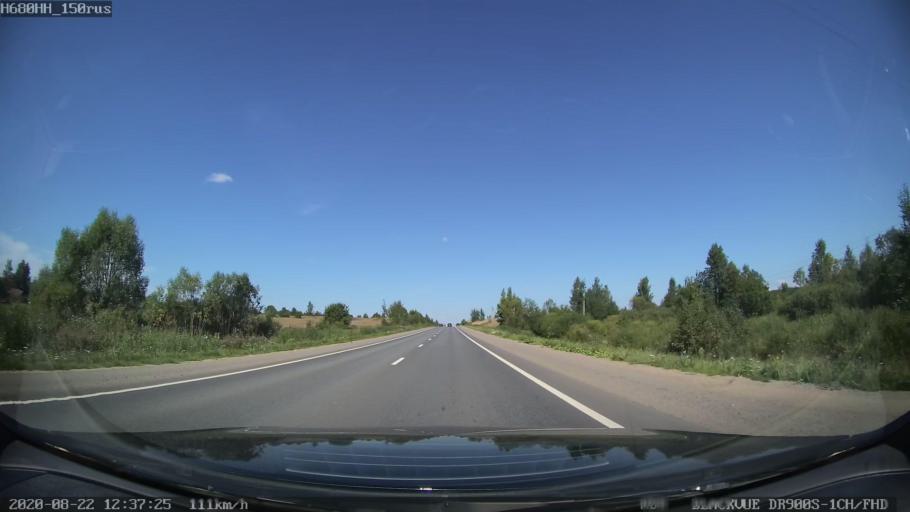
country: RU
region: Tverskaya
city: Rameshki
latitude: 57.2955
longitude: 36.0891
